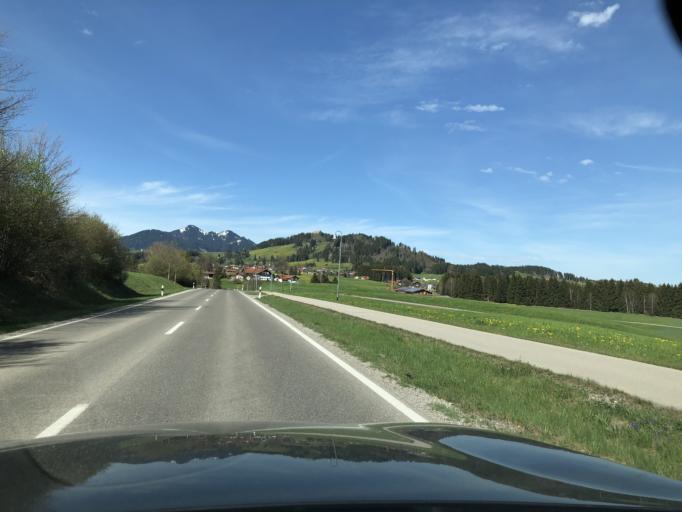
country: DE
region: Bavaria
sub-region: Swabia
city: Hopferau
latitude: 47.6133
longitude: 10.6297
